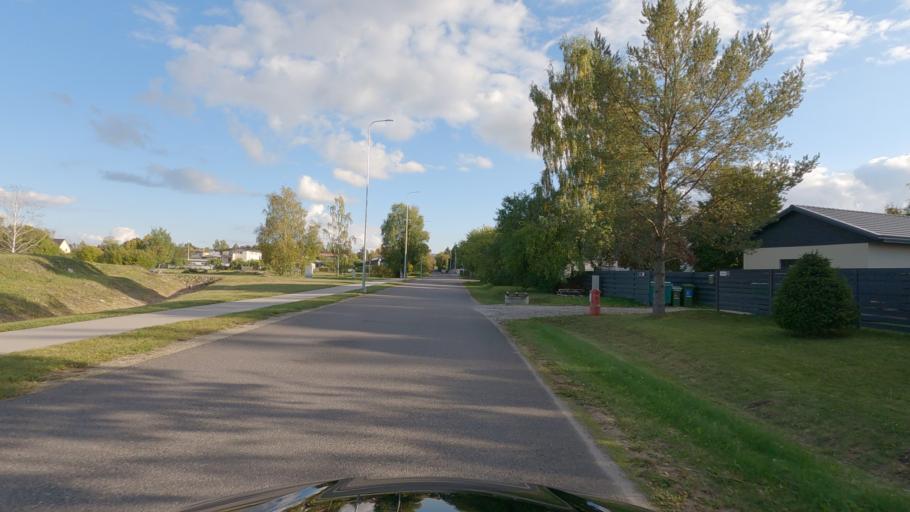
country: EE
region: Harju
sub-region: Saku vald
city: Saku
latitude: 59.3028
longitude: 24.6510
